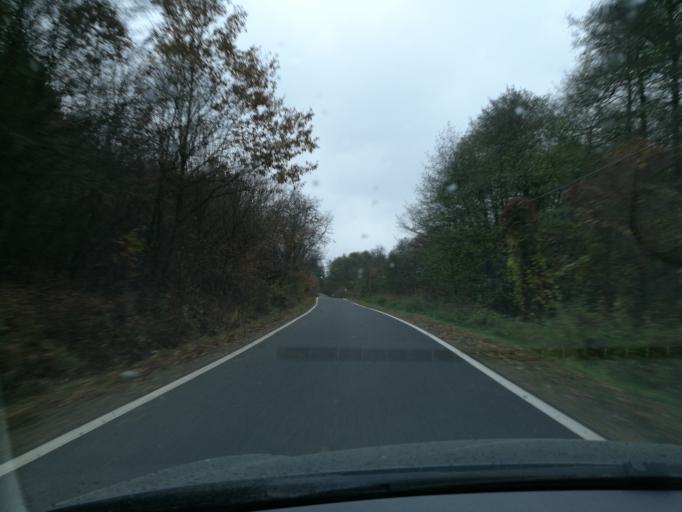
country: HU
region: Nograd
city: Paszto
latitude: 47.9701
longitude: 19.6225
